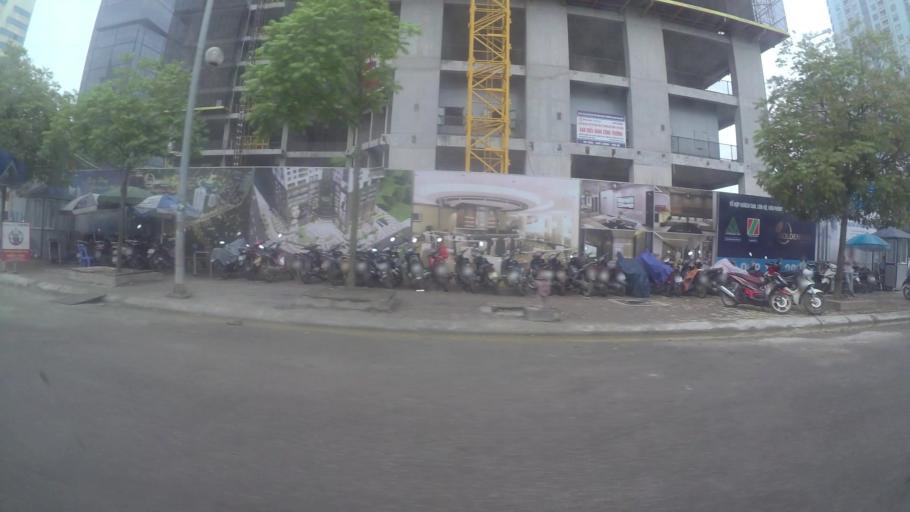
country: VN
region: Ha Noi
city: Cau Giay
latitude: 21.0238
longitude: 105.7907
